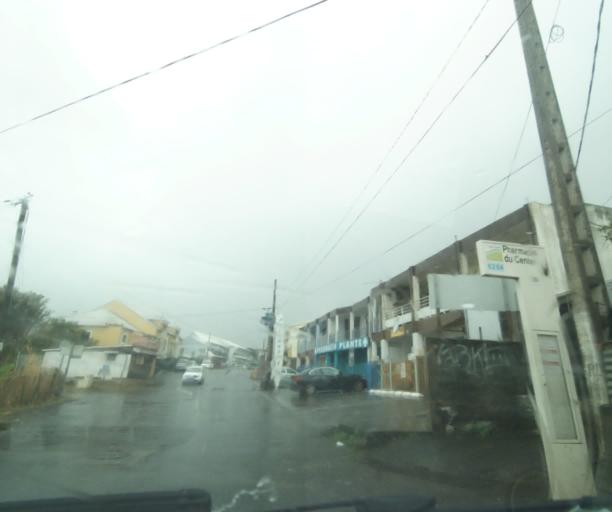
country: RE
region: Reunion
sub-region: Reunion
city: La Possession
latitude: -20.9835
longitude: 55.3263
